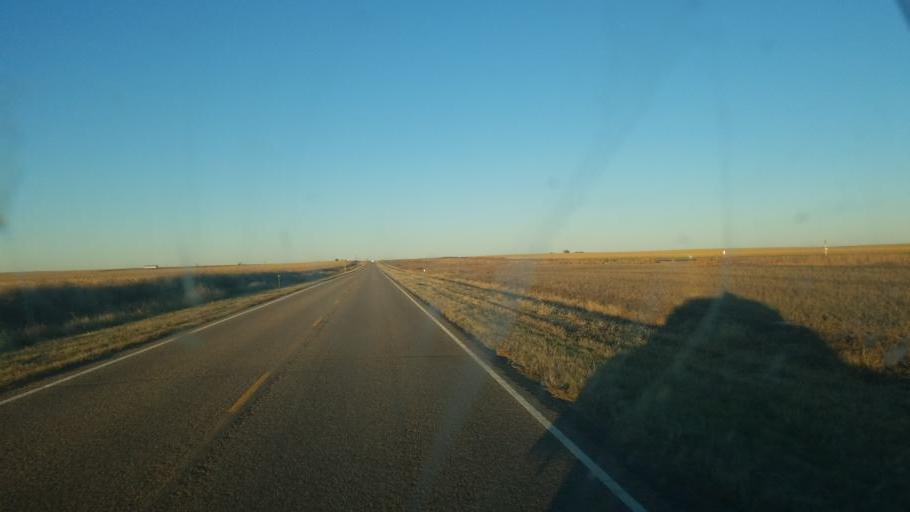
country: US
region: Colorado
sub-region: Cheyenne County
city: Cheyenne Wells
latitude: 38.8503
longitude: -102.0964
